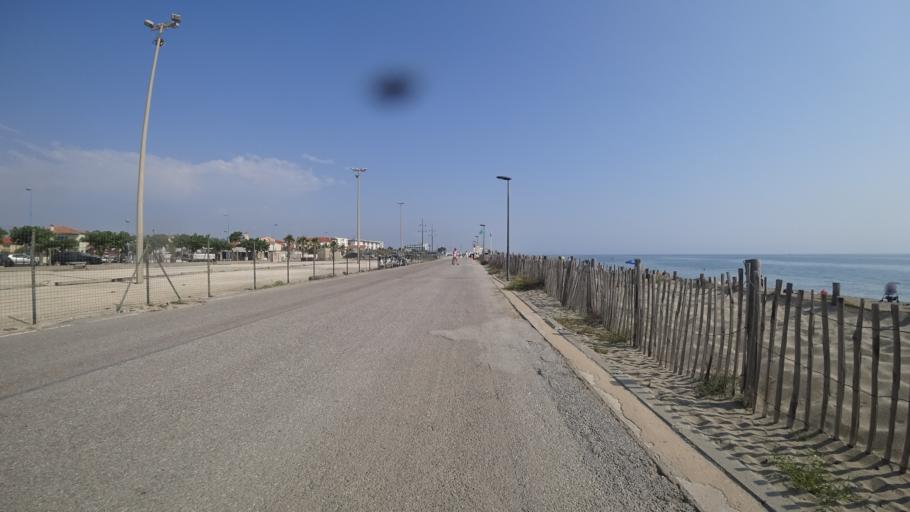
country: FR
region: Languedoc-Roussillon
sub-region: Departement des Pyrenees-Orientales
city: Saint-Cyprien-Plage
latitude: 42.6325
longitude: 3.0355
